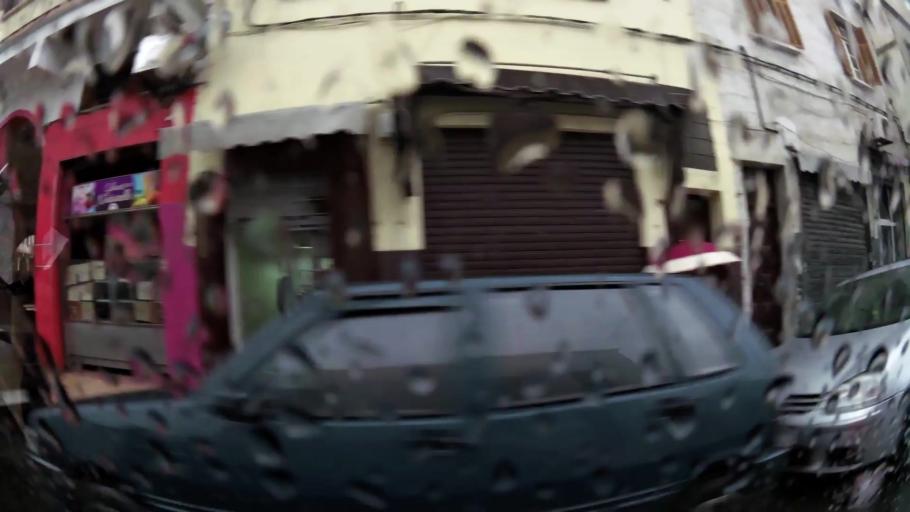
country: MA
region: Grand Casablanca
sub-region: Casablanca
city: Casablanca
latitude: 33.5701
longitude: -7.6059
